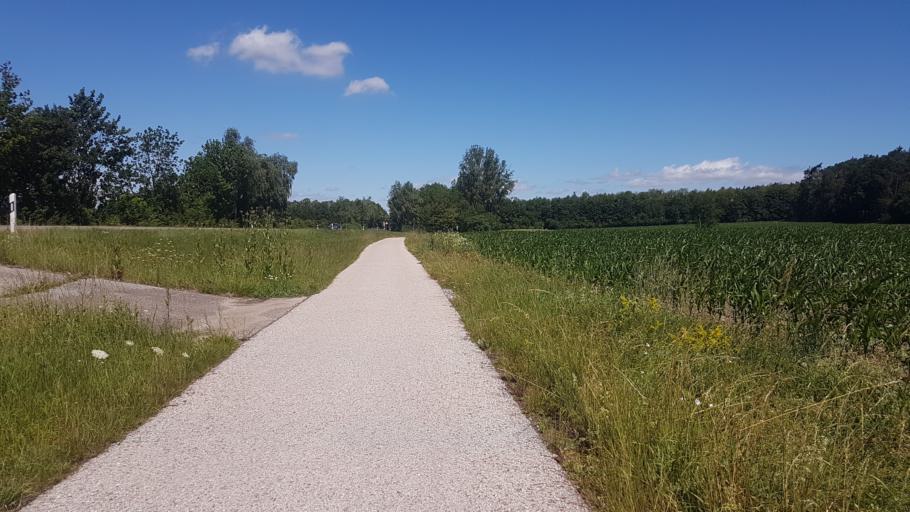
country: DE
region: Bavaria
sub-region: Regierungsbezirk Mittelfranken
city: Herrieden
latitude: 49.2460
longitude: 10.4678
